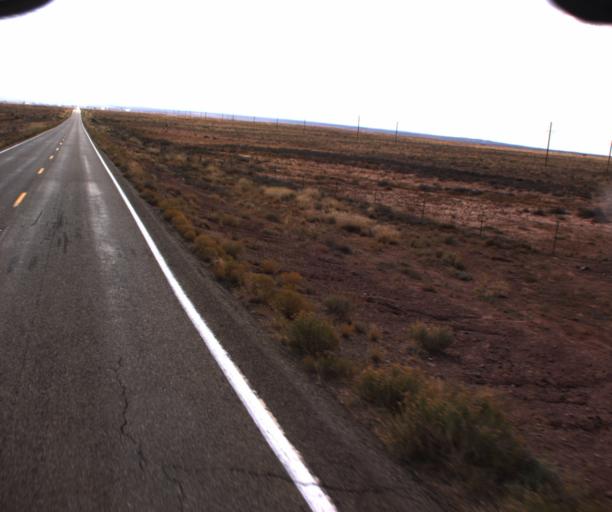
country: US
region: Arizona
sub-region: Apache County
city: Many Farms
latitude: 36.5375
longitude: -109.5179
